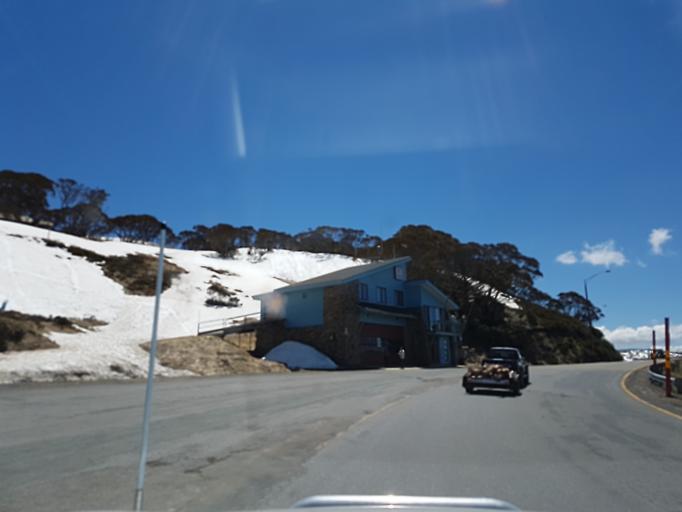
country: AU
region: Victoria
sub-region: Alpine
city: Mount Beauty
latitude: -36.9910
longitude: 147.1481
